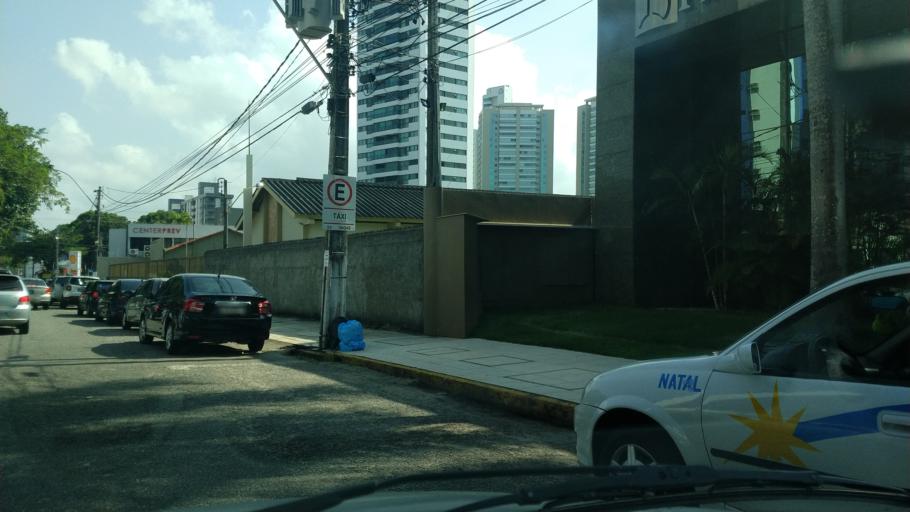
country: BR
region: Rio Grande do Norte
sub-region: Natal
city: Natal
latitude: -5.7904
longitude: -35.2009
